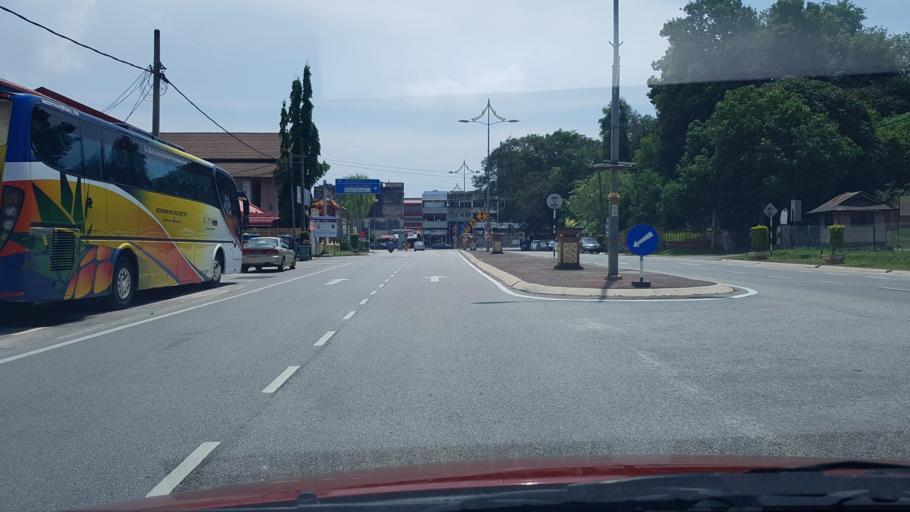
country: MY
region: Terengganu
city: Kuala Terengganu
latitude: 5.3295
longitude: 103.1328
